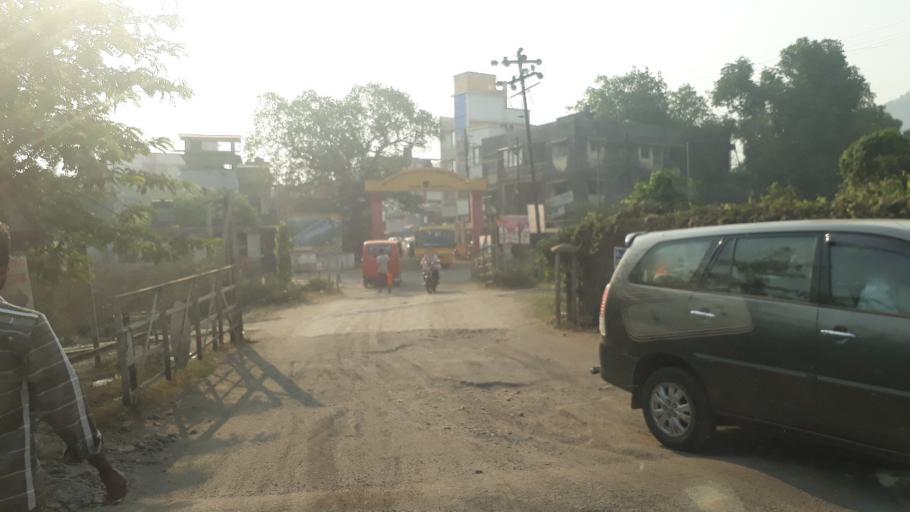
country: IN
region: Maharashtra
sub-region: Raigarh
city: Neral
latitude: 19.0232
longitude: 73.3173
